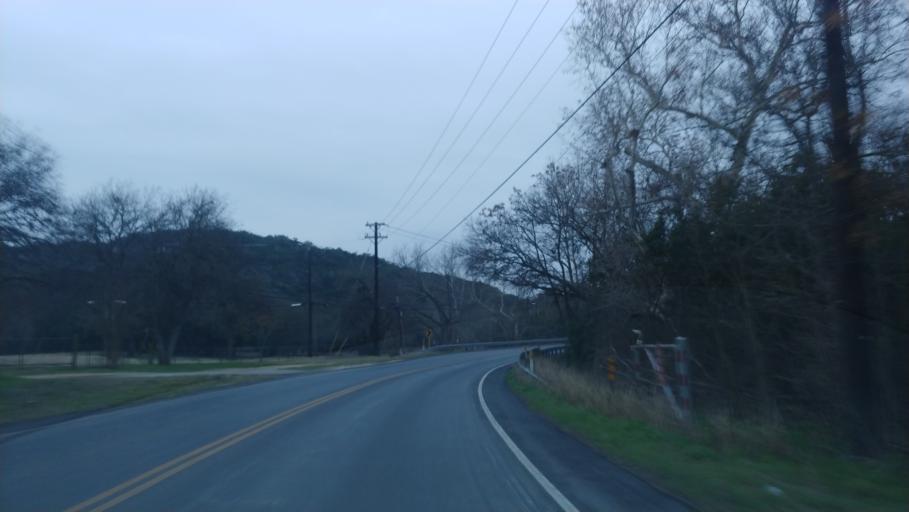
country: US
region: Texas
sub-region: Bexar County
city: Helotes
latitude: 29.5851
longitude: -98.6878
